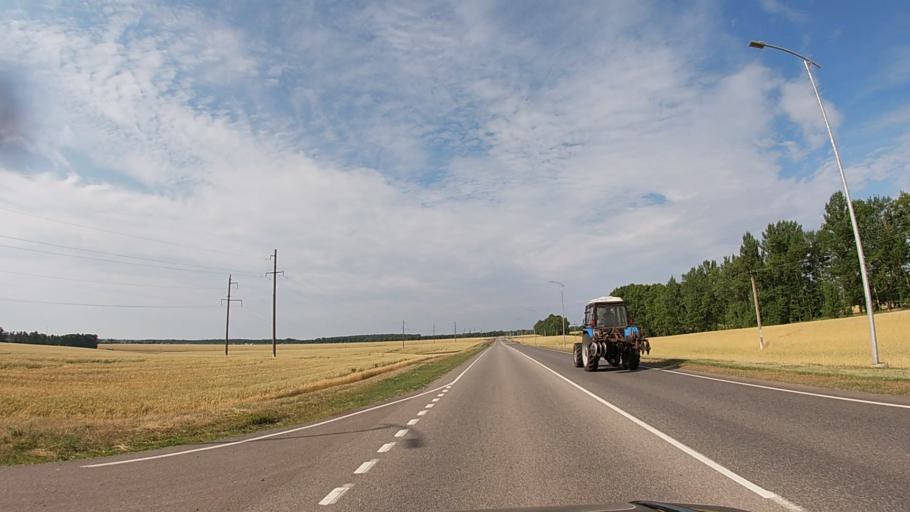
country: RU
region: Belgorod
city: Proletarskiy
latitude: 50.8132
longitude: 35.7496
